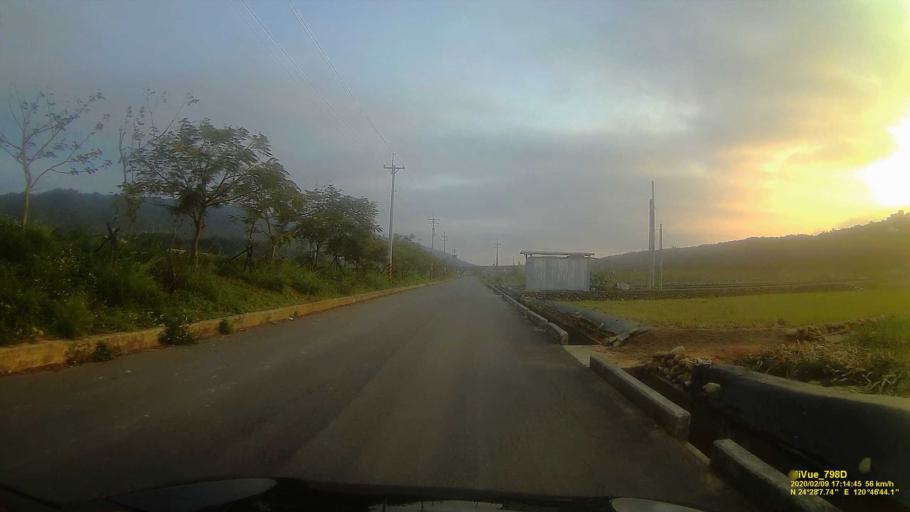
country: TW
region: Taiwan
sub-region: Miaoli
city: Miaoli
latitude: 24.4685
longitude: 120.7789
